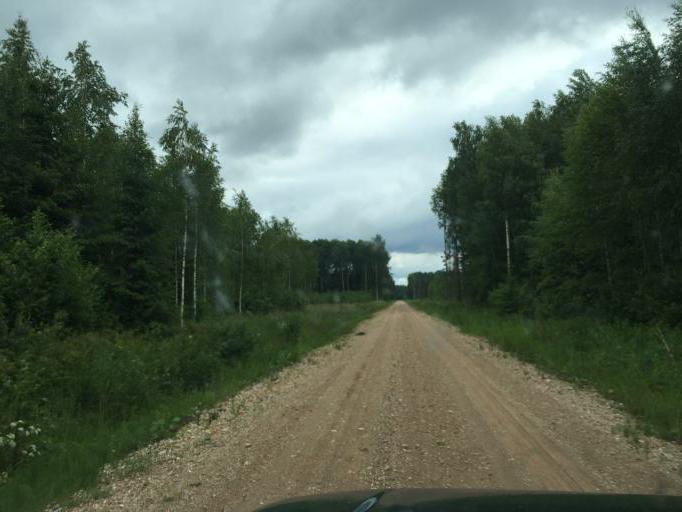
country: LV
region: Vilaka
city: Vilaka
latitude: 57.3872
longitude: 27.5026
